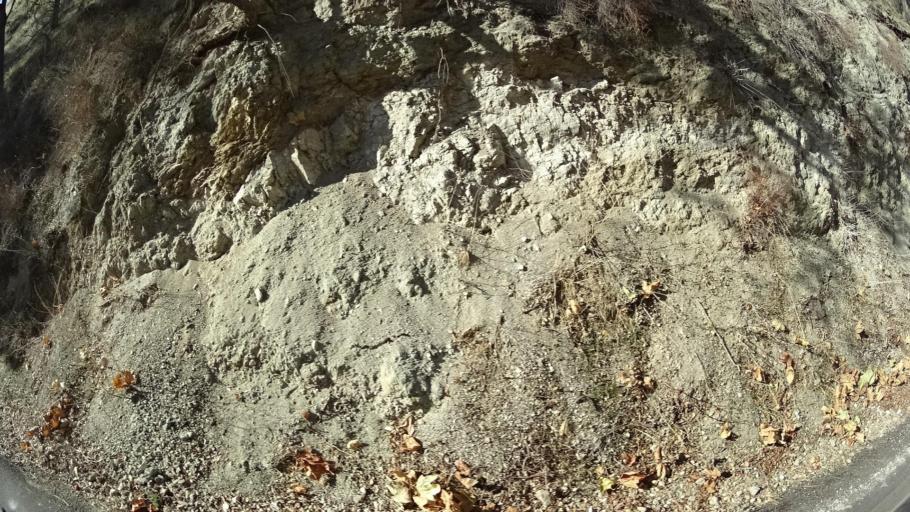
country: US
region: California
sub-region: Kern County
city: Bear Valley Springs
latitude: 35.3330
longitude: -118.5890
